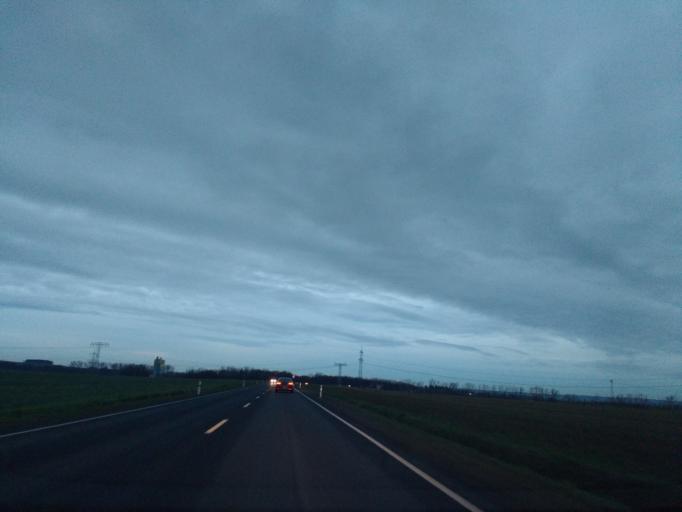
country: DE
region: Saxony-Anhalt
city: Quedlinburg
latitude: 51.7930
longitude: 11.1838
